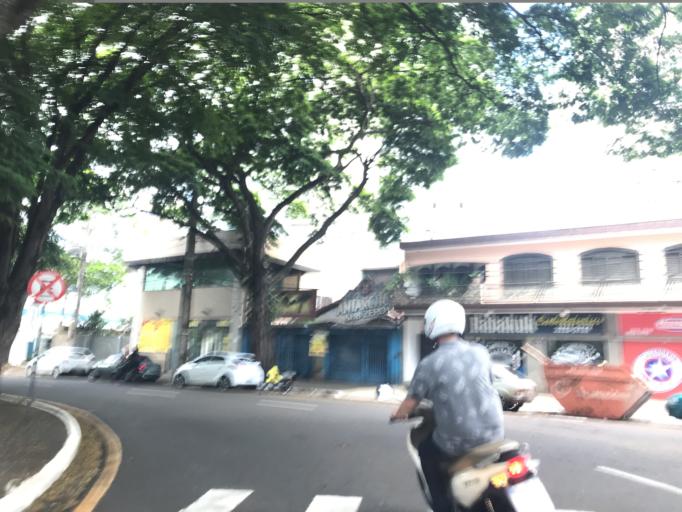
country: BR
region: Parana
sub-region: Maringa
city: Maringa
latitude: -23.4158
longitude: -51.9270
